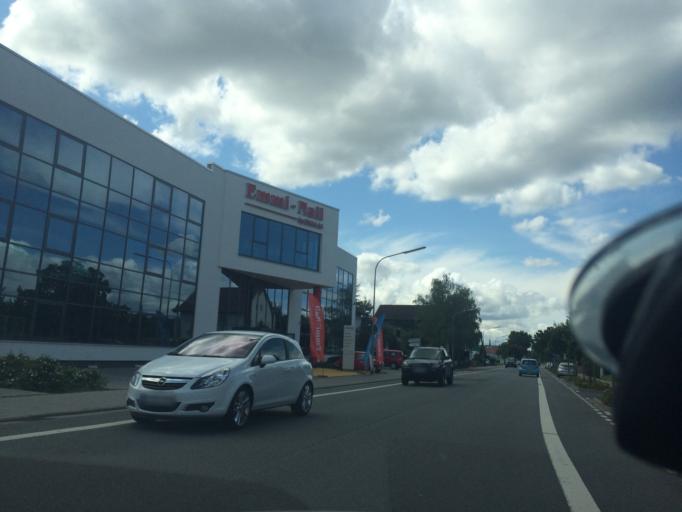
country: DE
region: Hesse
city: Morfelden-Walldorf
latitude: 49.9700
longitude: 8.5662
